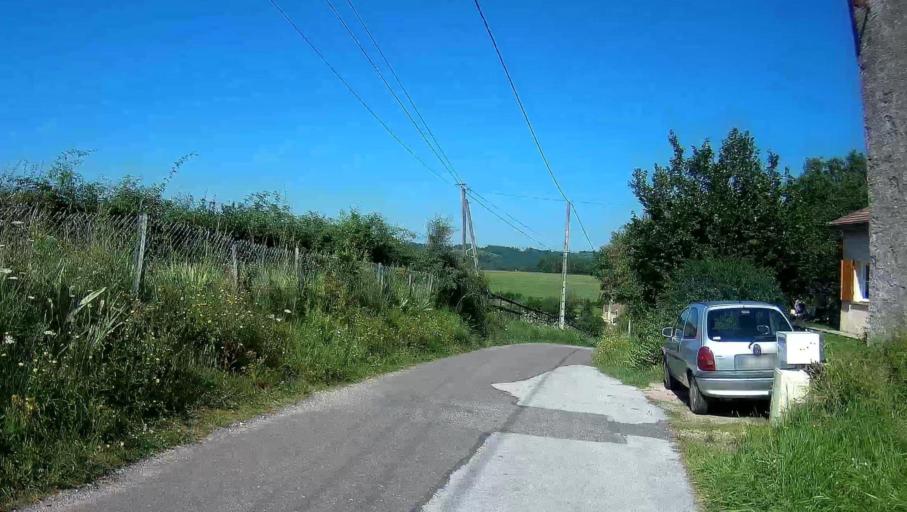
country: FR
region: Bourgogne
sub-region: Departement de Saone-et-Loire
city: Couches
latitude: 46.8421
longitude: 4.5777
